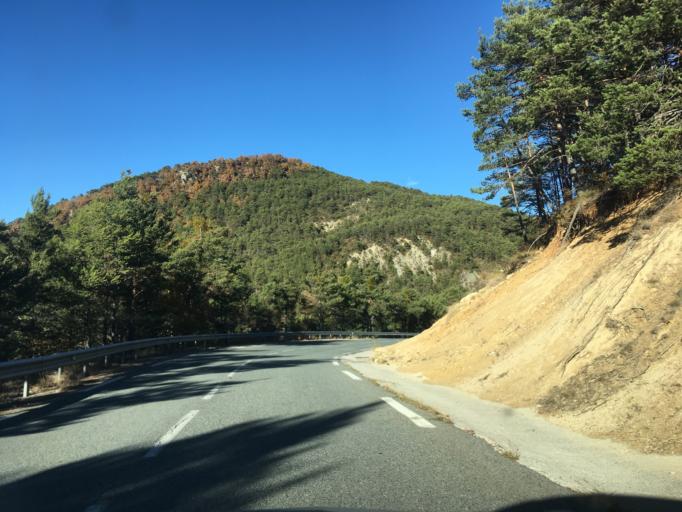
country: FR
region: Provence-Alpes-Cote d'Azur
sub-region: Departement des Alpes-de-Haute-Provence
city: Castellane
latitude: 43.7352
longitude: 6.5024
